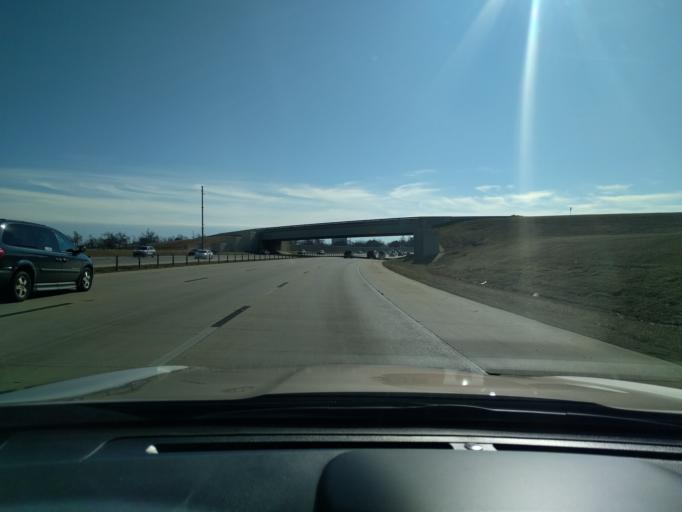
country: US
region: Oklahoma
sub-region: Oklahoma County
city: Nichols Hills
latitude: 35.5458
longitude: -97.5757
